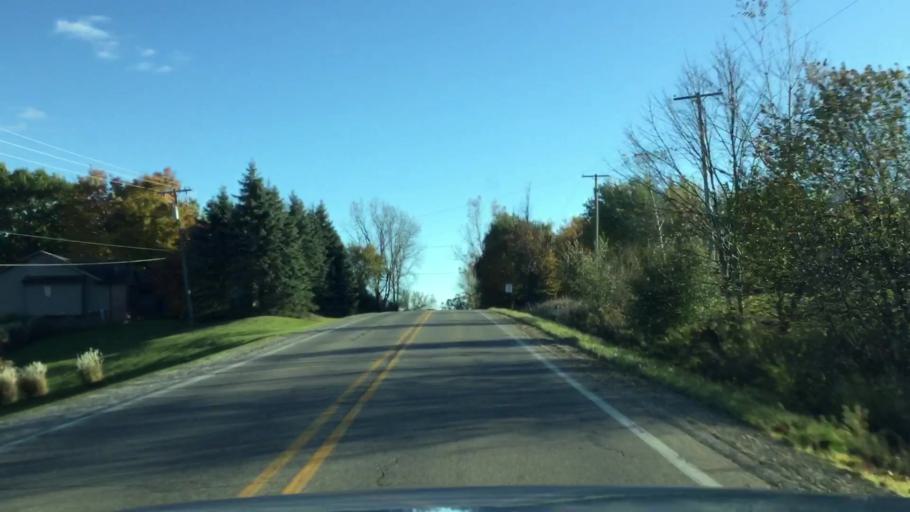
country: US
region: Michigan
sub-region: Lapeer County
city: Imlay City
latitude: 43.0425
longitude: -83.1672
